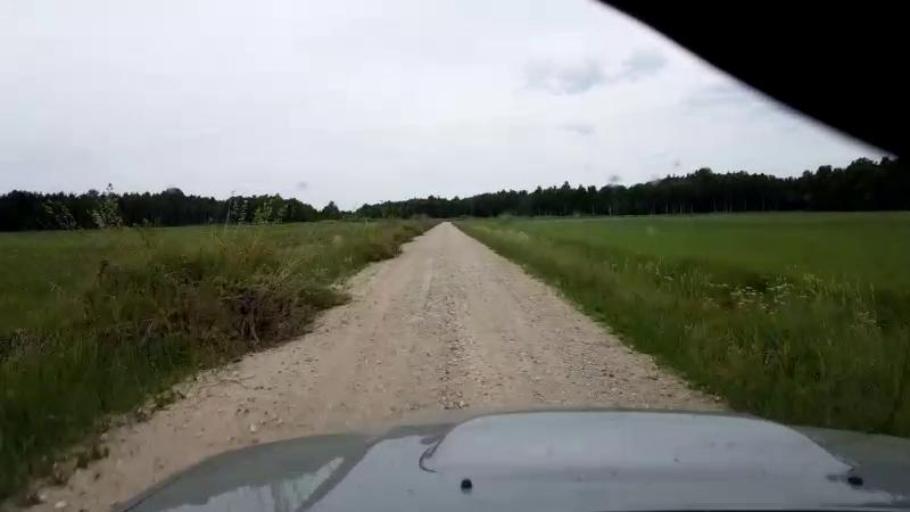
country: EE
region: Paernumaa
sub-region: Halinga vald
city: Parnu-Jaagupi
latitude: 58.5432
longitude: 24.6010
